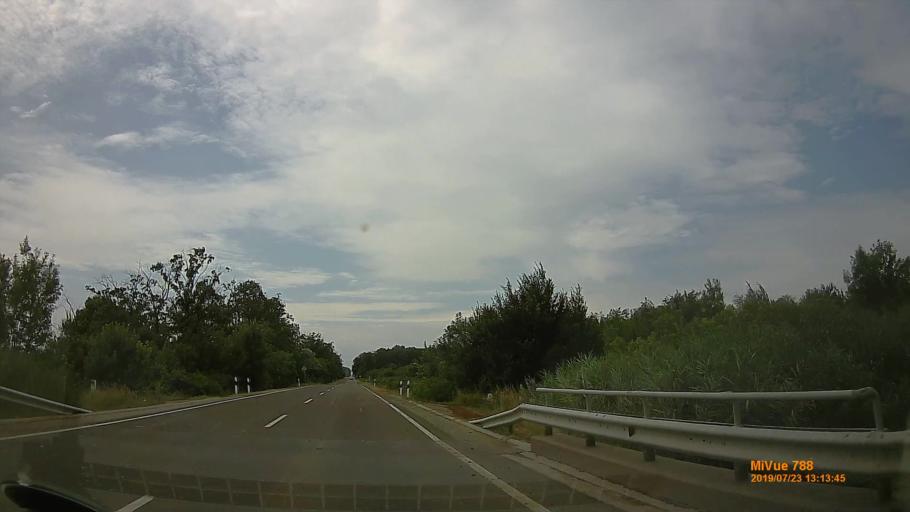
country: HU
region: Hajdu-Bihar
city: Gorbehaza
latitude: 47.9231
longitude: 21.2246
